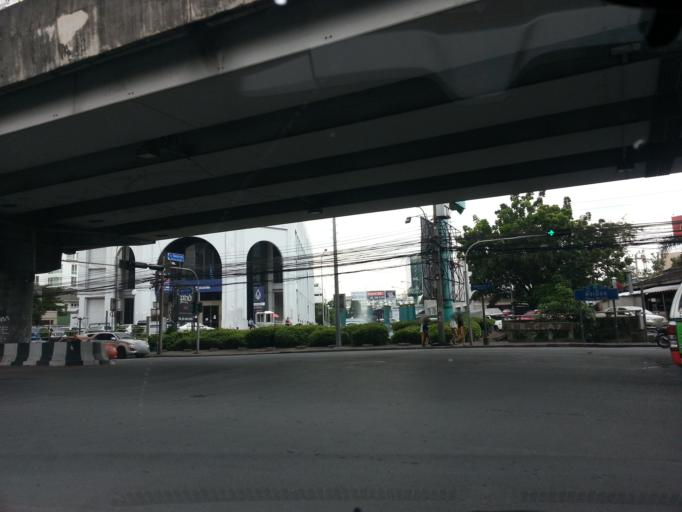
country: TH
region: Bangkok
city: Huai Khwang
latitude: 13.7556
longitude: 100.5733
